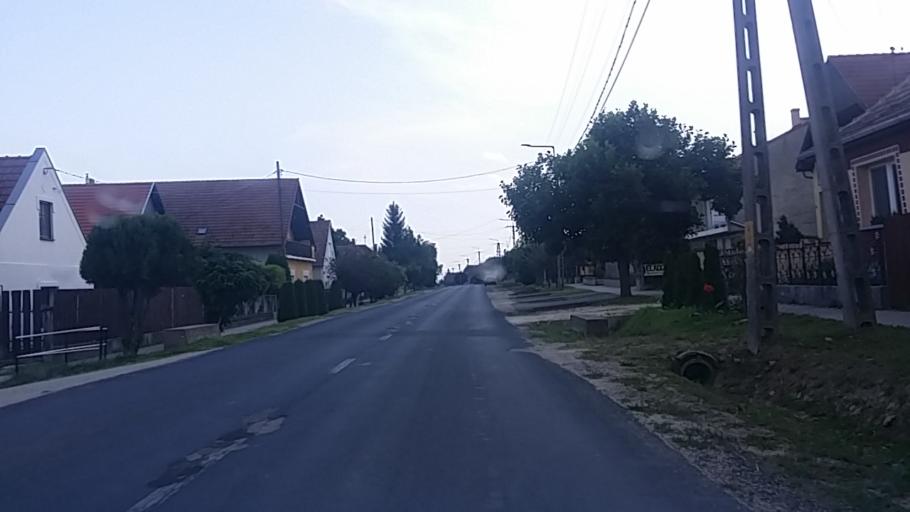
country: HU
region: Zala
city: Heviz
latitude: 46.7671
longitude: 17.1722
